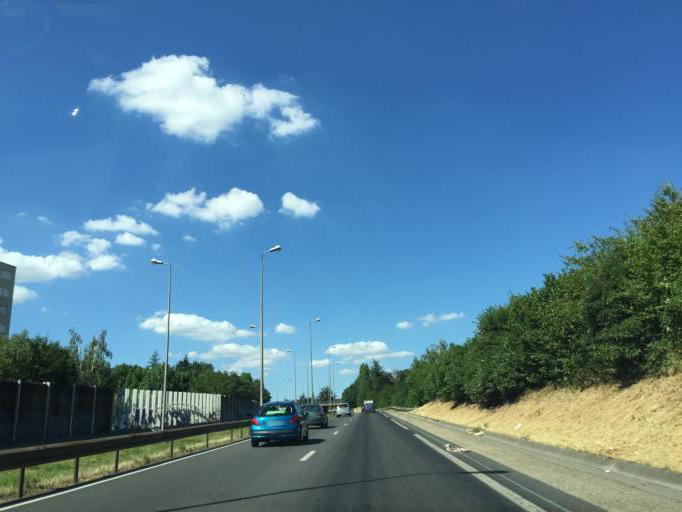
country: FR
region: Rhone-Alpes
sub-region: Departement de la Loire
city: Saint-Etienne
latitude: 45.4257
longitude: 4.4149
